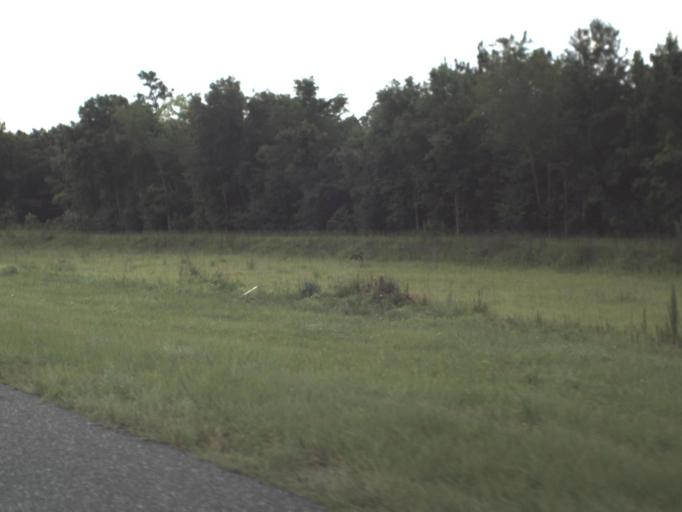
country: US
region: Florida
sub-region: Levy County
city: Inglis
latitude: 29.2092
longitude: -82.6962
